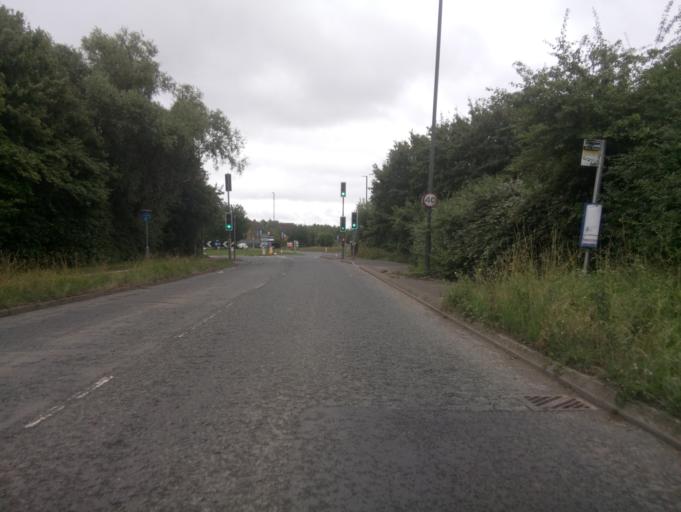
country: GB
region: England
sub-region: Gloucestershire
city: Tewkesbury
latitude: 51.9814
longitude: -2.1451
